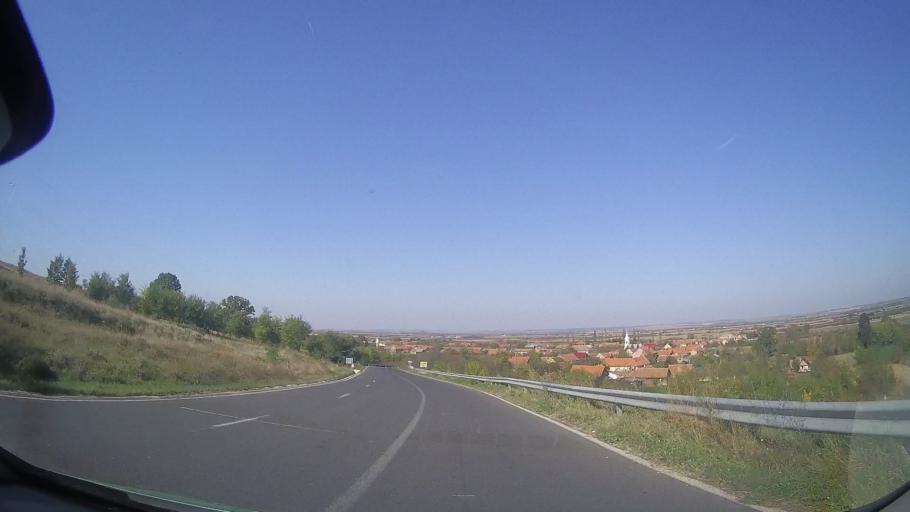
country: RO
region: Timis
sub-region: Comuna Costeiu
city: Costeiu
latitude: 45.7736
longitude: 21.8518
